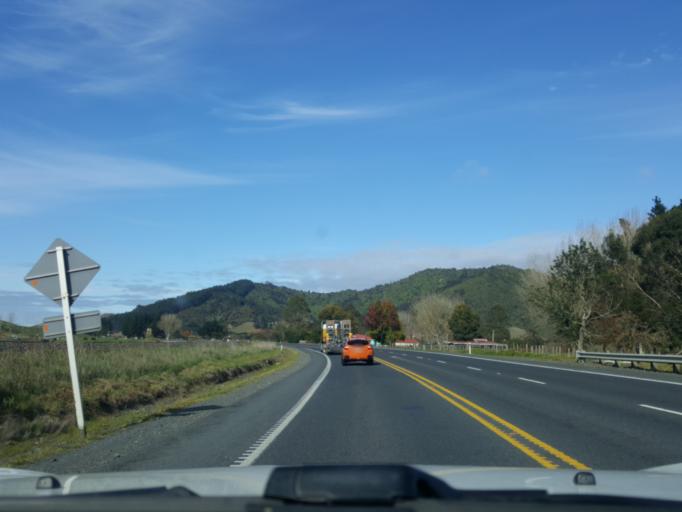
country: NZ
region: Waikato
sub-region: Waikato District
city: Ngaruawahia
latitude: -37.5914
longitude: 175.1594
